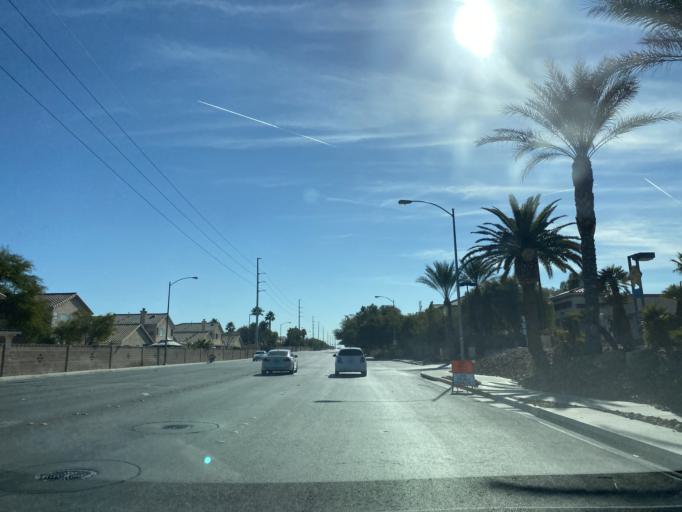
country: US
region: Nevada
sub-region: Clark County
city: North Las Vegas
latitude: 36.2392
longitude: -115.1437
